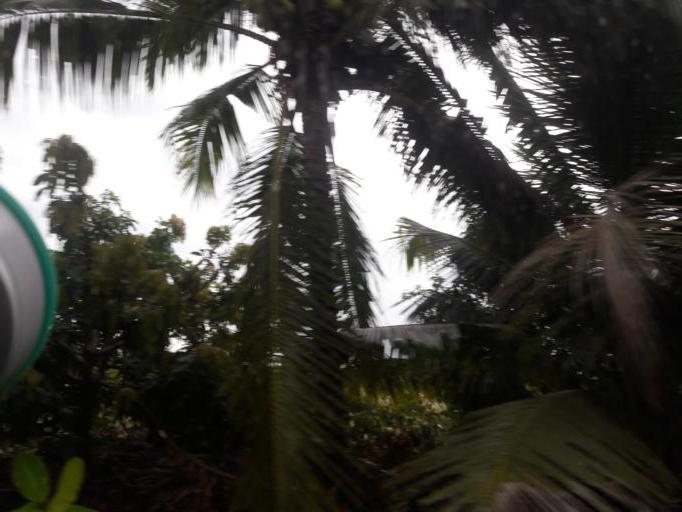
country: TH
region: Ratchaburi
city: Damnoen Saduak
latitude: 13.5319
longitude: 100.0143
